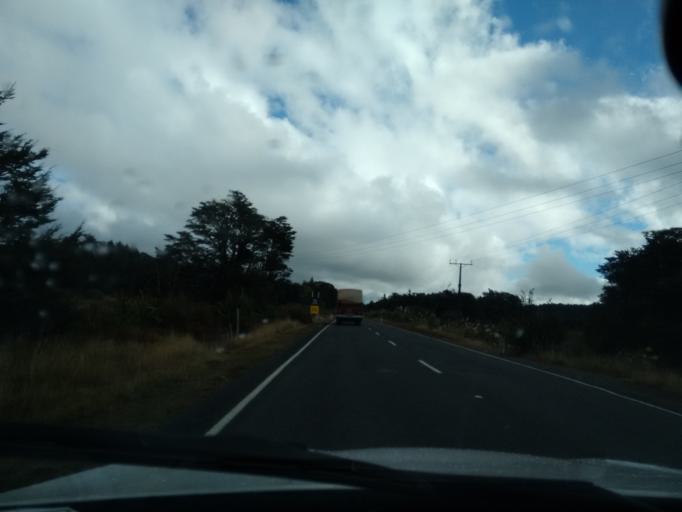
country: NZ
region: Manawatu-Wanganui
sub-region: Ruapehu District
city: Waiouru
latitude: -39.1694
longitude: 175.4805
